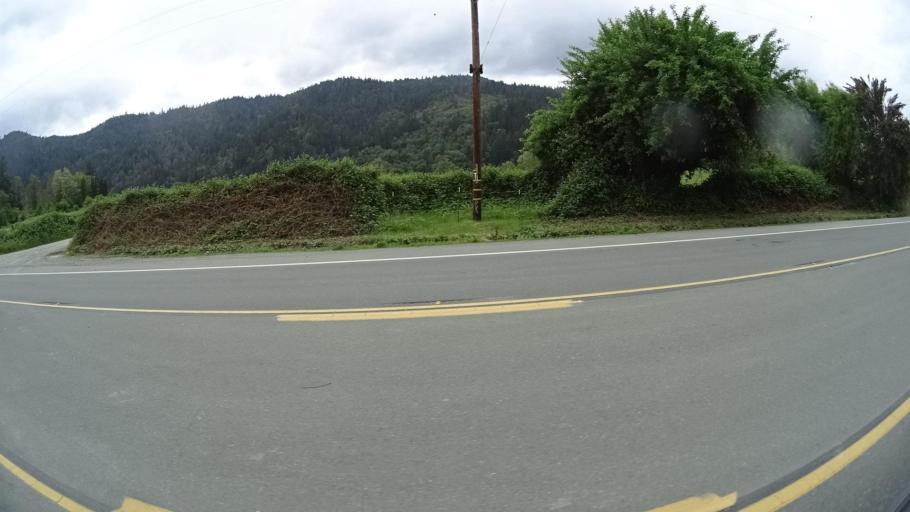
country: US
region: California
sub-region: Humboldt County
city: Willow Creek
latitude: 41.0688
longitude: -123.6868
